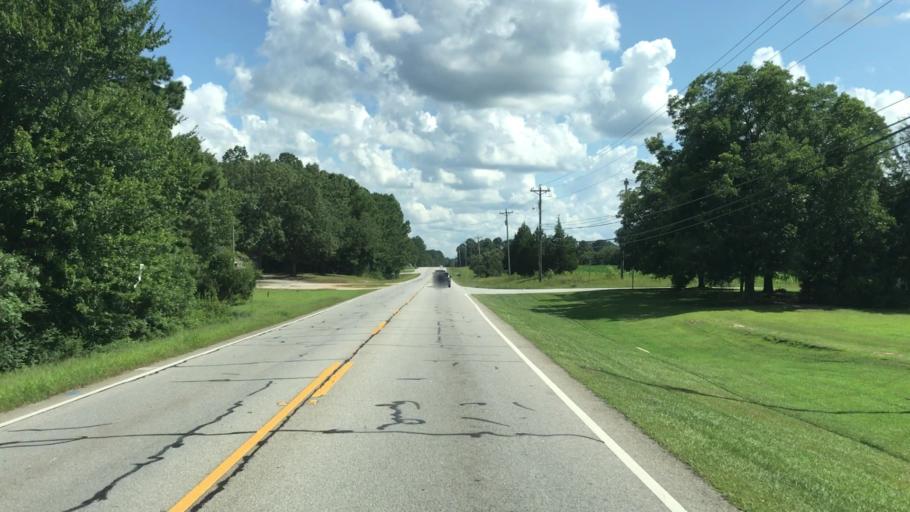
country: US
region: Georgia
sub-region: Walton County
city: Walnut Grove
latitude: 33.7714
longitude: -83.8519
